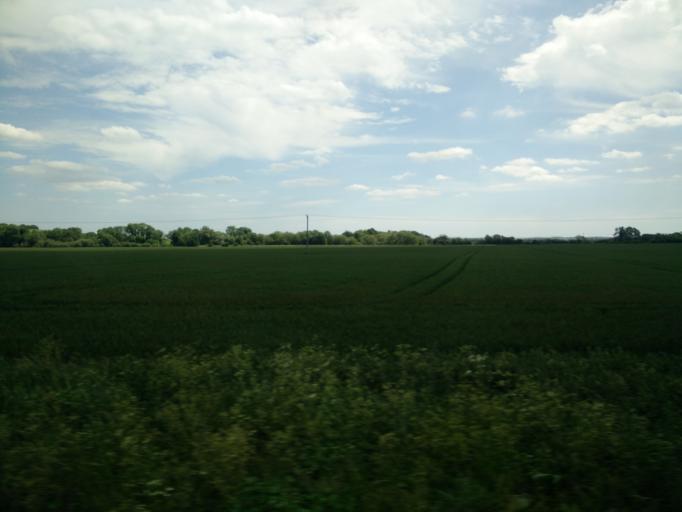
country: GB
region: England
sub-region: Cambridgeshire
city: Harston
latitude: 52.1241
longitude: 0.0601
